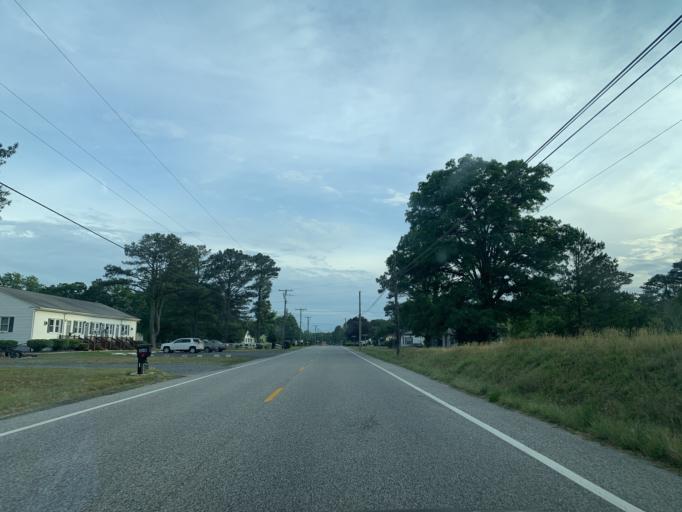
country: US
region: Maryland
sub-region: Worcester County
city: Snow Hill
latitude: 38.1487
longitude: -75.4119
